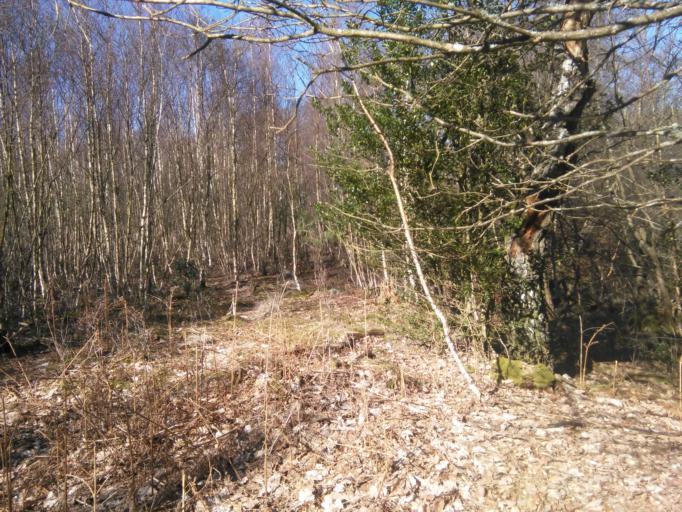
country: DK
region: Central Jutland
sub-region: Skanderborg Kommune
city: Ry
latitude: 56.1099
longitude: 9.7187
